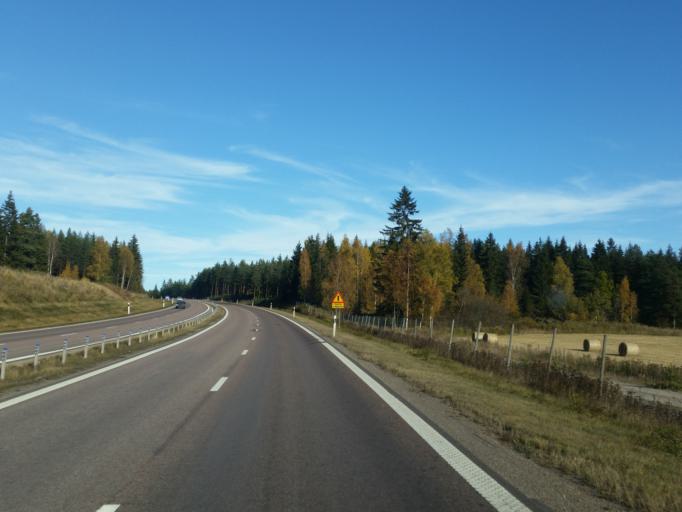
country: SE
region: Dalarna
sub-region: Borlange Kommun
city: Ornas
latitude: 60.5179
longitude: 15.5501
